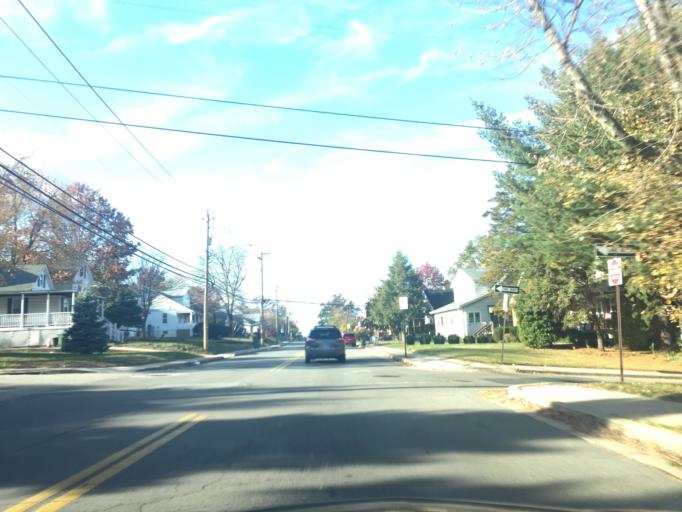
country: US
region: Maryland
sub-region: Baltimore County
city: Parkville
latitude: 39.3707
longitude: -76.5390
